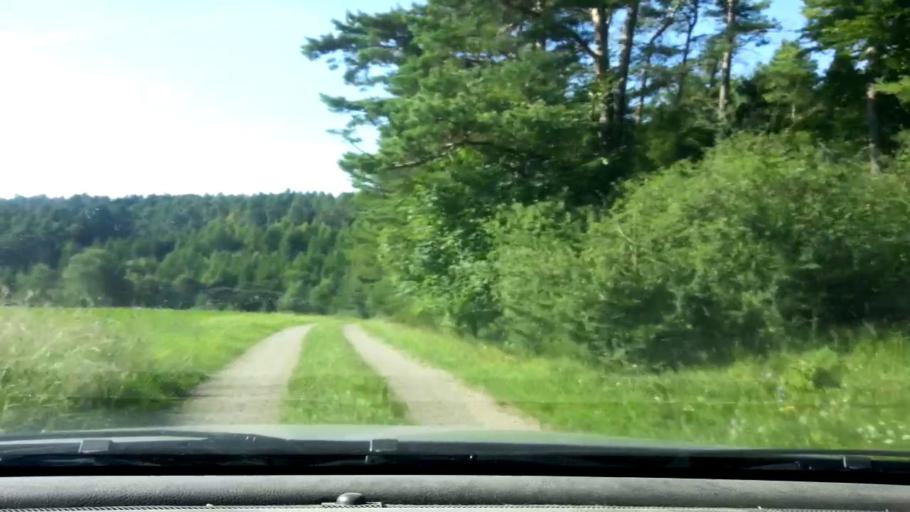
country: DE
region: Bavaria
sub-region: Upper Franconia
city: Wattendorf
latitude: 50.0030
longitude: 11.1102
